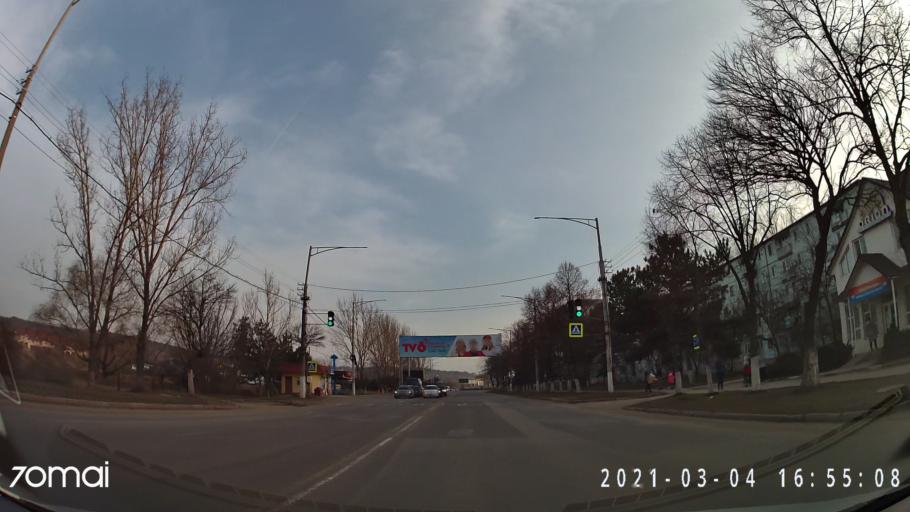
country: MD
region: Balti
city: Balti
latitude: 47.7585
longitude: 27.9409
